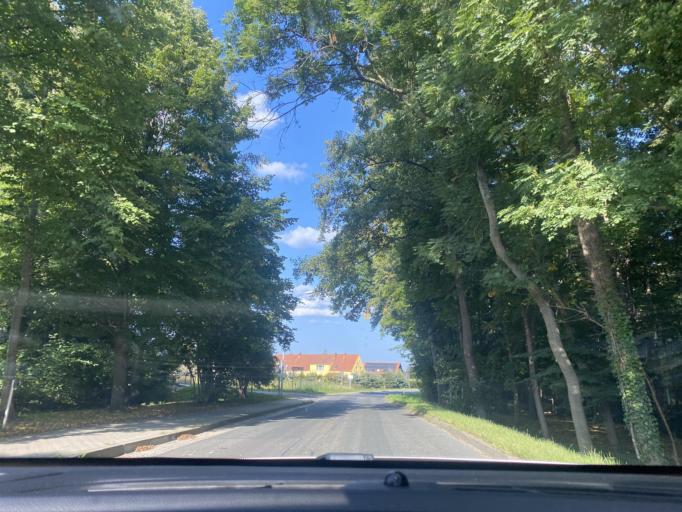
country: DE
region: Saxony
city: Quitzdorf
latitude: 51.2459
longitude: 14.7672
